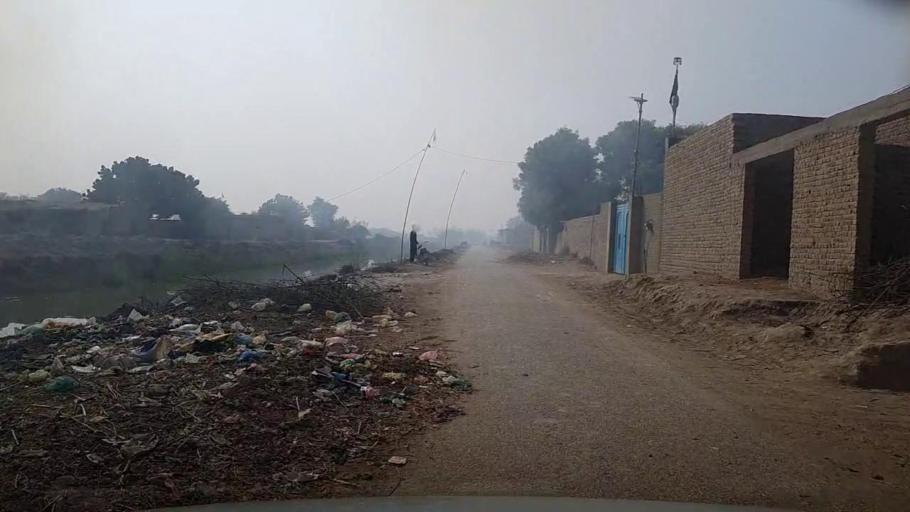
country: PK
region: Sindh
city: Setharja Old
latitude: 27.1979
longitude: 68.4815
